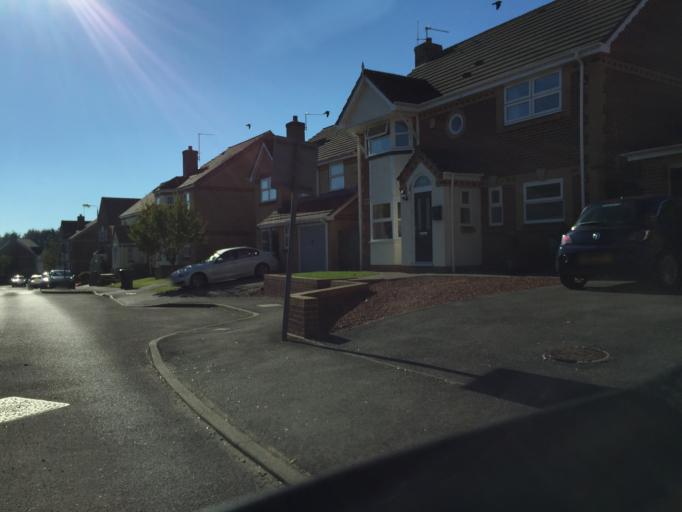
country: GB
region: England
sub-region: Wiltshire
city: Chippenham
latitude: 51.4698
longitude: -2.1396
